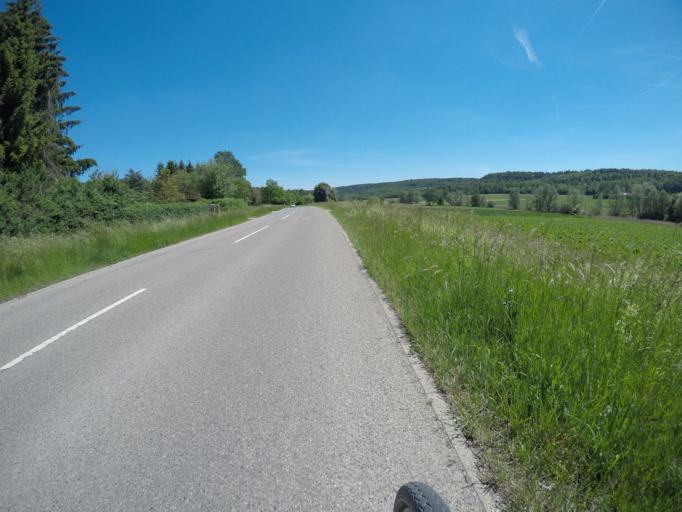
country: DE
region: Baden-Wuerttemberg
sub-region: Regierungsbezirk Stuttgart
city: Magstadt
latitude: 48.7448
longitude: 8.9833
